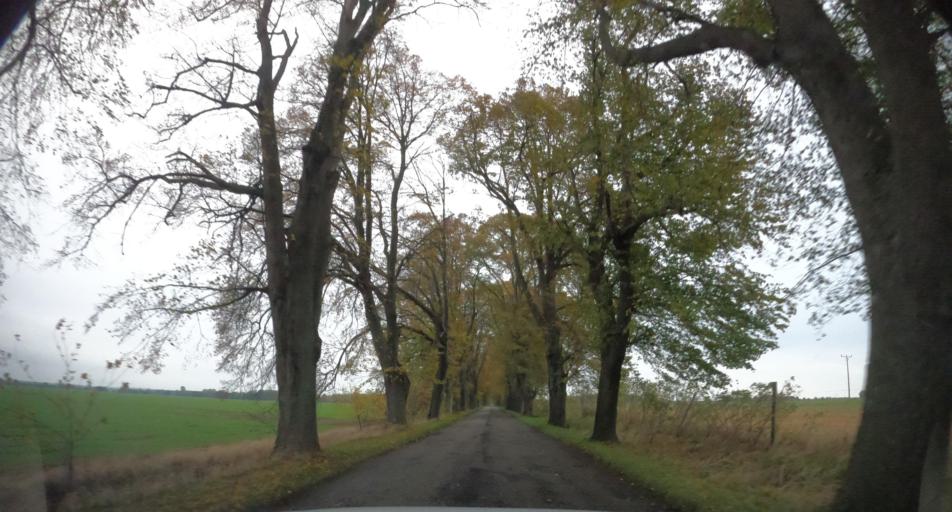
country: PL
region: West Pomeranian Voivodeship
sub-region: Powiat kamienski
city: Wolin
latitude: 53.9003
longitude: 14.6284
